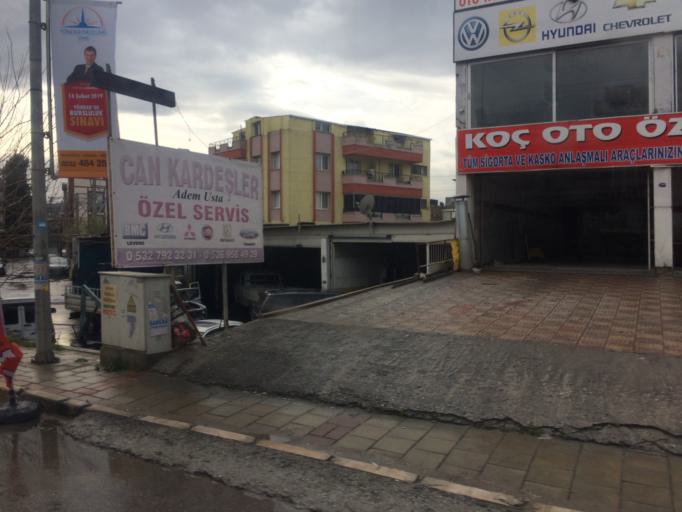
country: TR
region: Izmir
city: Karsiyaka
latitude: 38.5175
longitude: 27.0411
